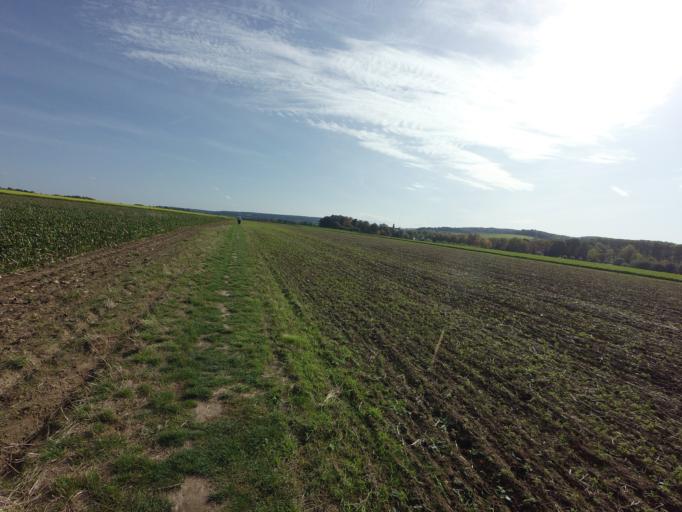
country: NL
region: Limburg
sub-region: Gemeente Voerendaal
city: Ubachsberg
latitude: 50.8192
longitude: 5.9114
